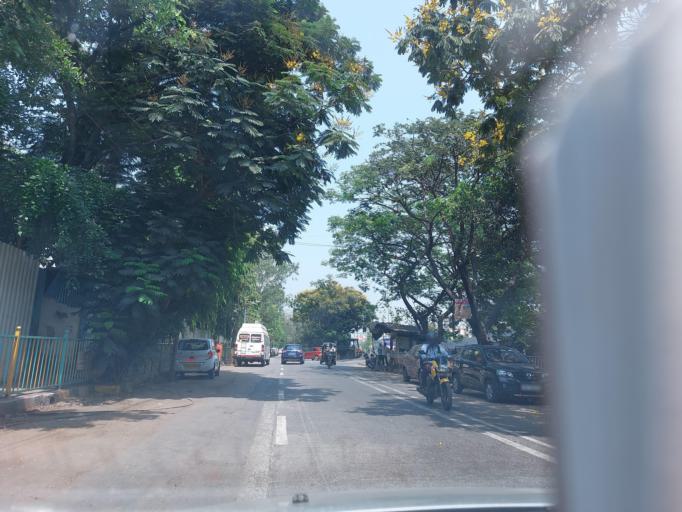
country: IN
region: Maharashtra
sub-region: Mumbai Suburban
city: Mumbai
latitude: 19.0503
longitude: 72.8726
